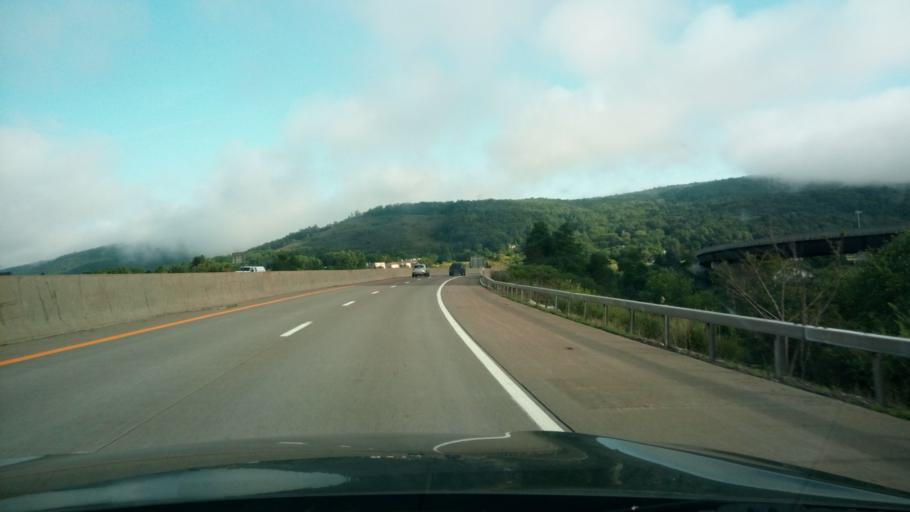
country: US
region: New York
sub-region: Steuben County
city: Corning
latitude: 42.1560
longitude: -77.0547
